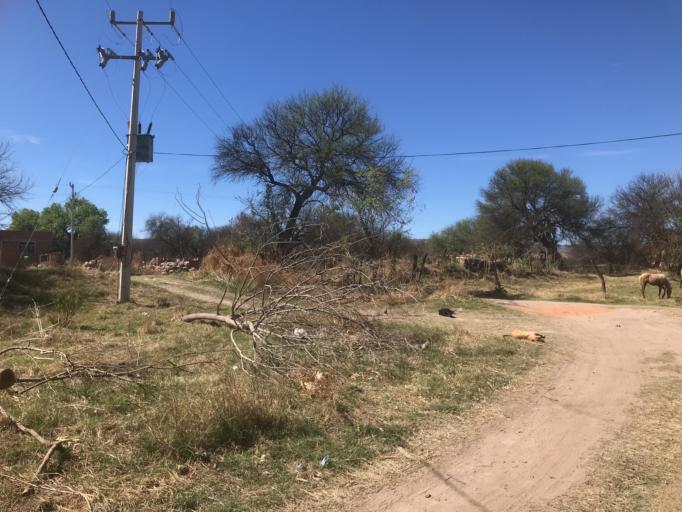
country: MX
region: Durango
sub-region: Durango
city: Sebastian Lerdo de Tejada
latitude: 23.9754
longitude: -104.6168
